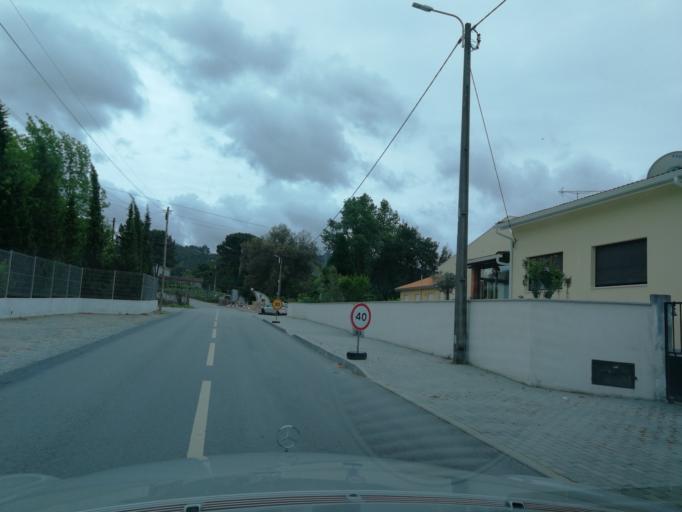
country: PT
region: Braga
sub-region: Braga
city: Adaufe
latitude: 41.6011
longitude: -8.3806
